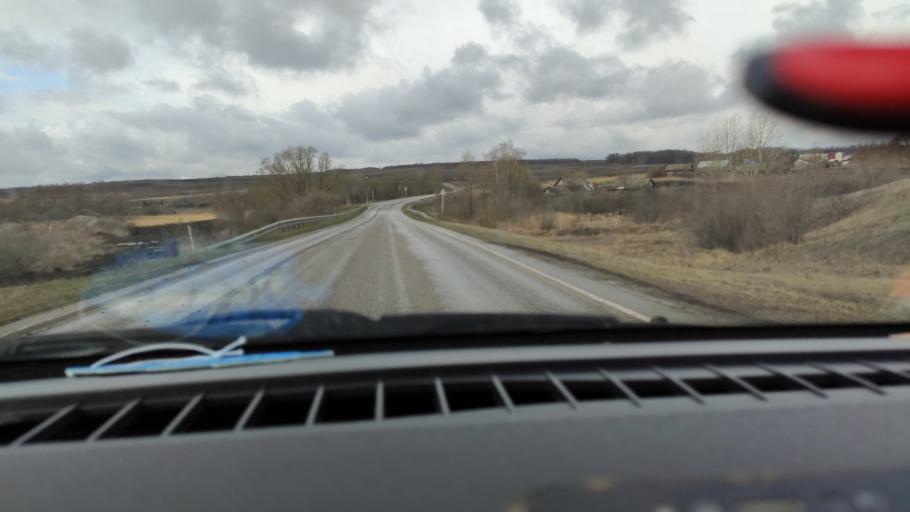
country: RU
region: Tatarstan
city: Nurlat
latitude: 54.3637
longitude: 50.6843
